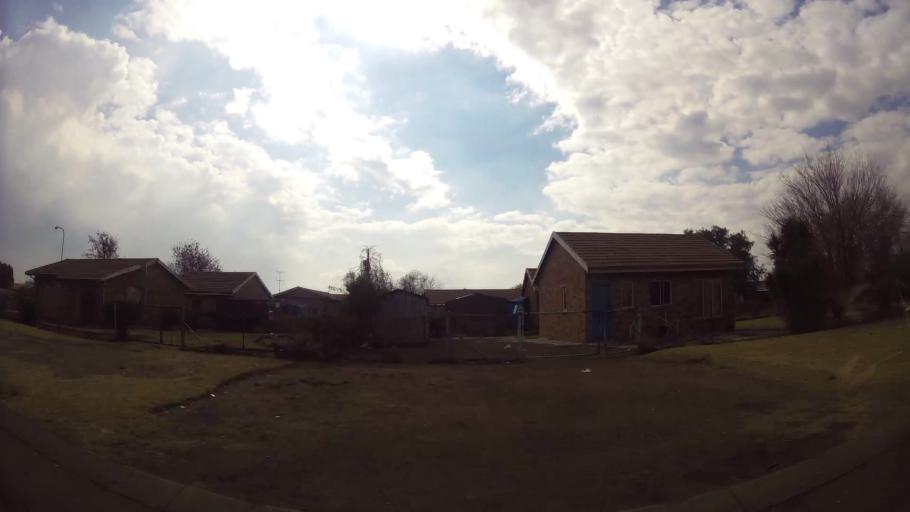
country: ZA
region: Gauteng
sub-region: Sedibeng District Municipality
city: Vereeniging
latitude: -26.6661
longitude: 27.9149
